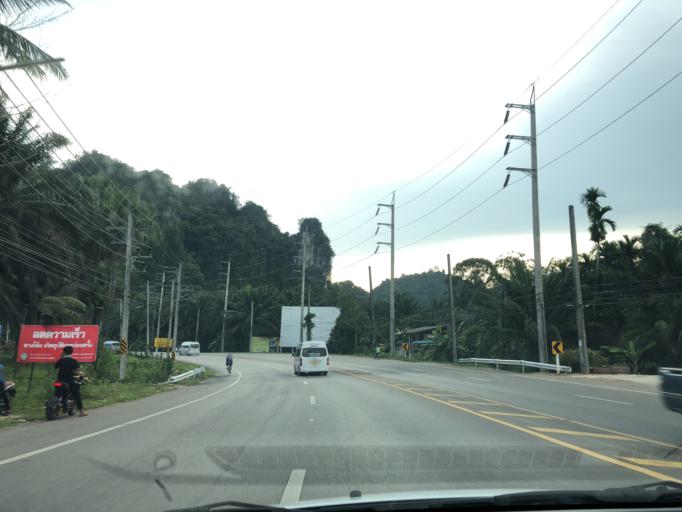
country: TH
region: Krabi
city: Krabi
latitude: 8.0871
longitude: 98.8810
